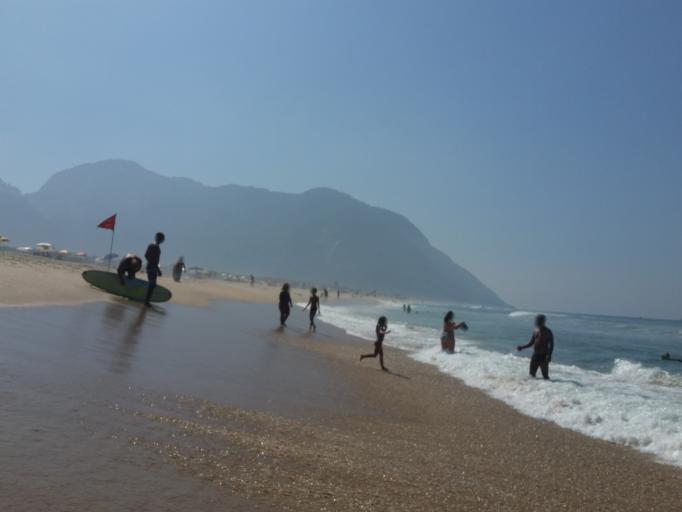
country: BR
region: Rio de Janeiro
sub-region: Nilopolis
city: Nilopolis
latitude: -23.0508
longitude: -43.5350
